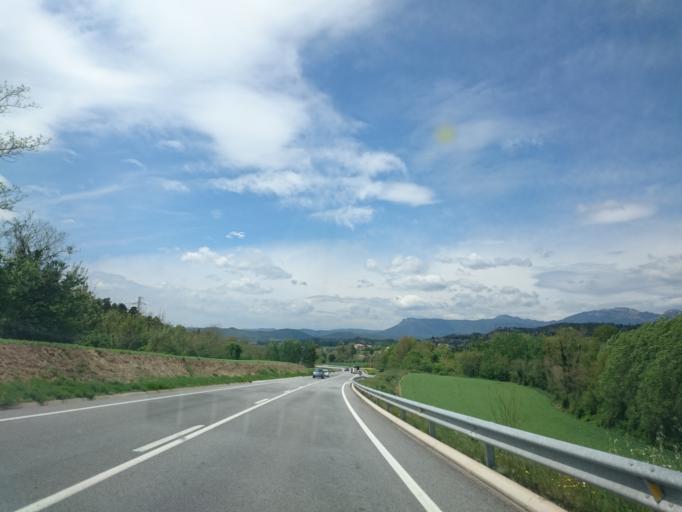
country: ES
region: Catalonia
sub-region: Provincia de Barcelona
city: Olvan
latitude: 42.0520
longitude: 1.9153
